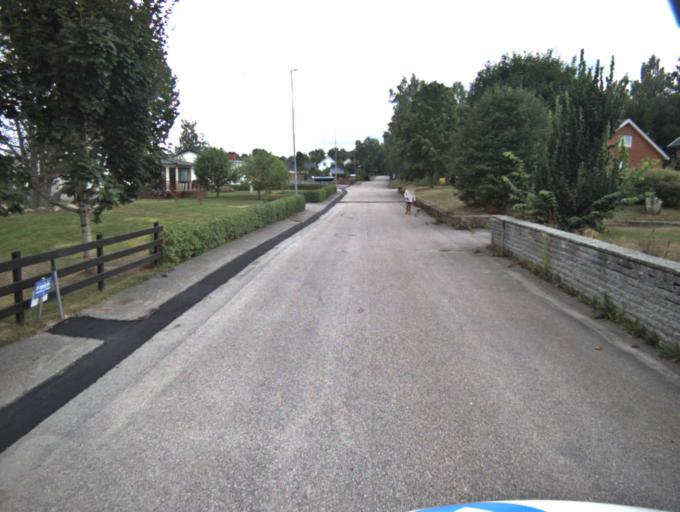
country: SE
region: Vaestra Goetaland
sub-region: Ulricehamns Kommun
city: Ulricehamn
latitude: 57.6764
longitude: 13.3707
